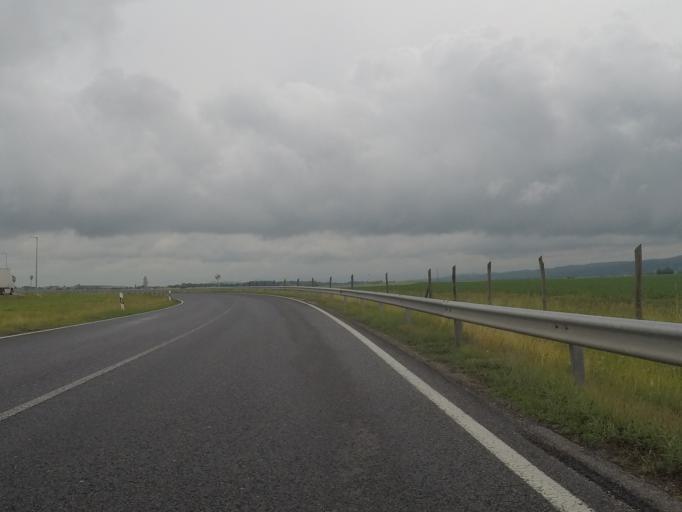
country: HU
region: Gyor-Moson-Sopron
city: Gyorujbarat
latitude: 47.6332
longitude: 17.6602
